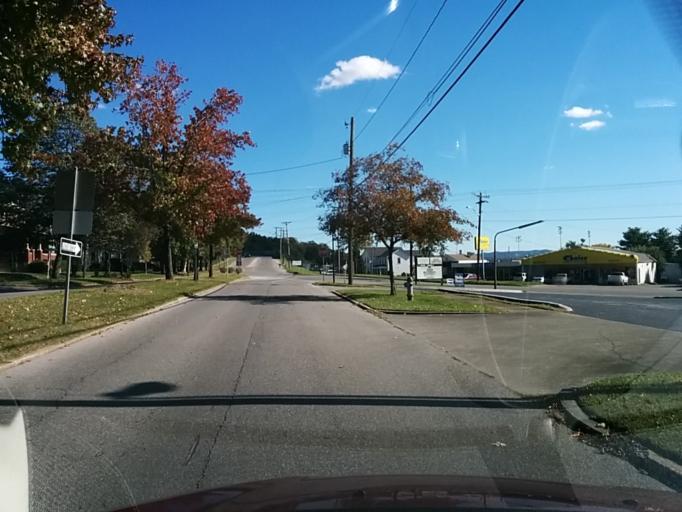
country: US
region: Virginia
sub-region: City of Salem
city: Salem
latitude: 37.2880
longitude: -80.0500
